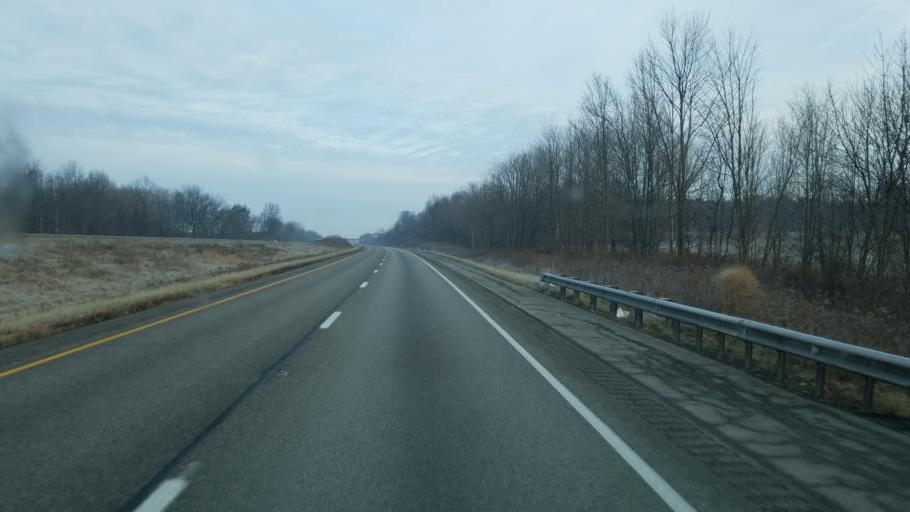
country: US
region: Pennsylvania
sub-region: Mercer County
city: Stoneboro
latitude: 41.3038
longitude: -80.1577
